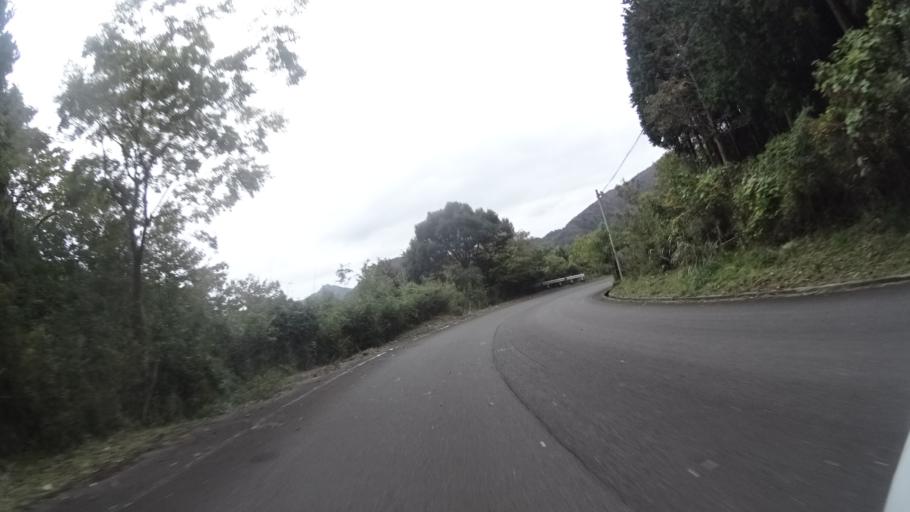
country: JP
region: Kyoto
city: Maizuru
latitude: 35.5675
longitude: 135.4629
